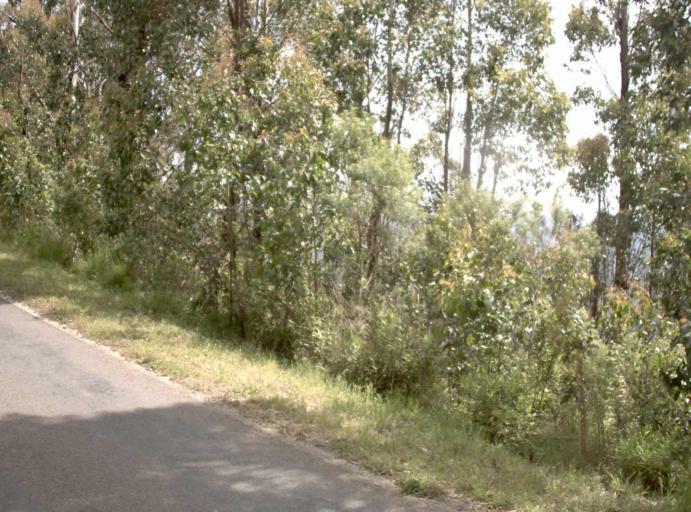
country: AU
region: Victoria
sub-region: Latrobe
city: Traralgon
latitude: -38.3934
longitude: 146.5554
